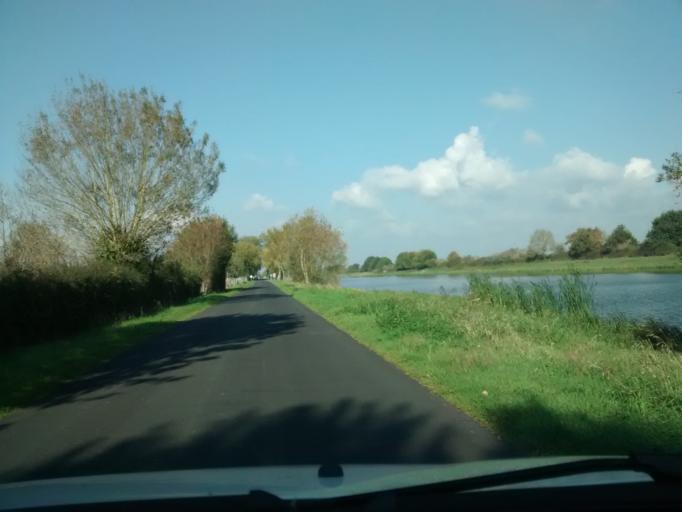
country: FR
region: Pays de la Loire
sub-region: Departement de la Loire-Atlantique
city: Frossay
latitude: 47.2537
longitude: -1.9057
